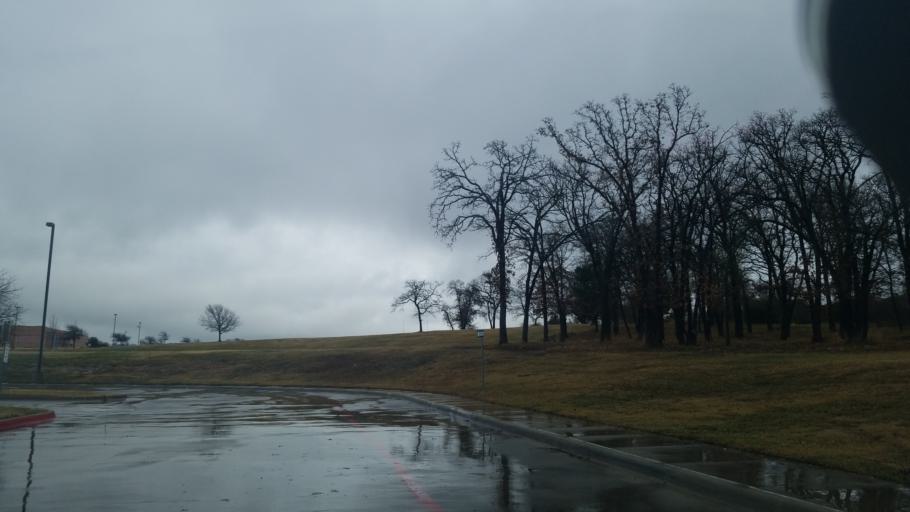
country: US
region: Texas
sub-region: Denton County
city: Corinth
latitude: 33.1463
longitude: -97.0849
